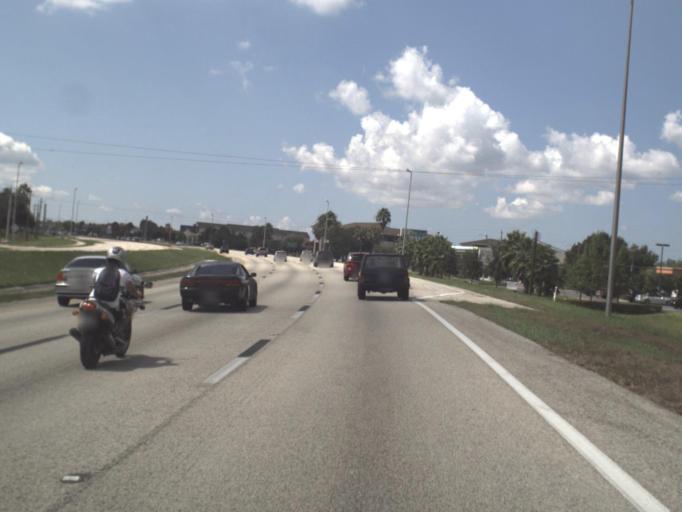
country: US
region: Florida
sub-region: Lee County
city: Fort Myers
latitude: 26.6123
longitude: -81.8174
